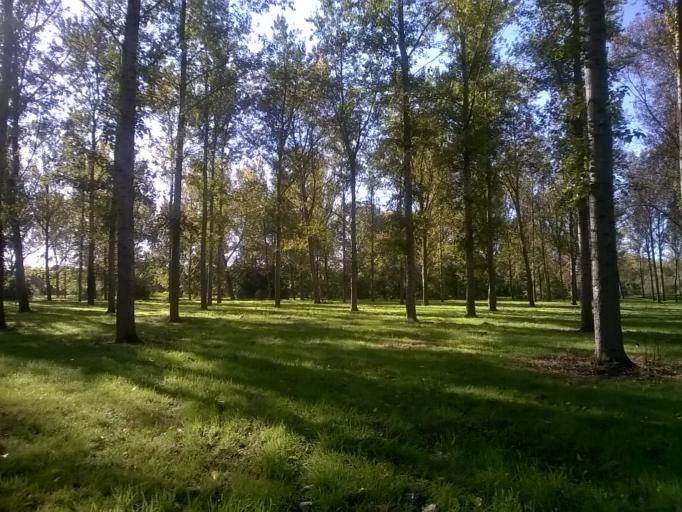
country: GB
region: England
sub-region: Milton Keynes
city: Broughton
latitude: 52.0462
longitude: -0.7177
